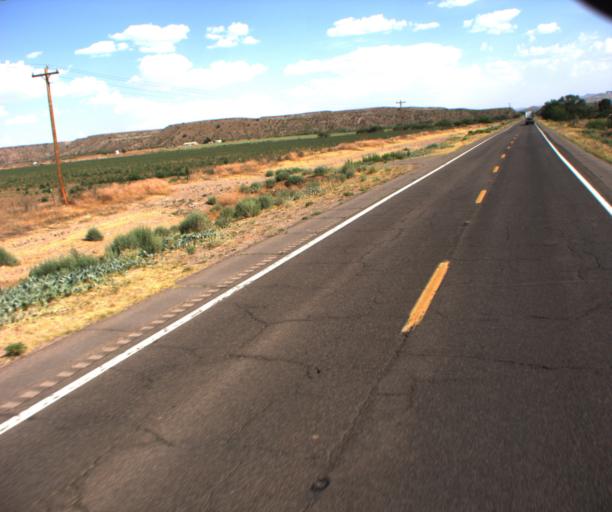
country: US
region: Arizona
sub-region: Greenlee County
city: Clifton
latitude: 32.8540
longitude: -109.1821
